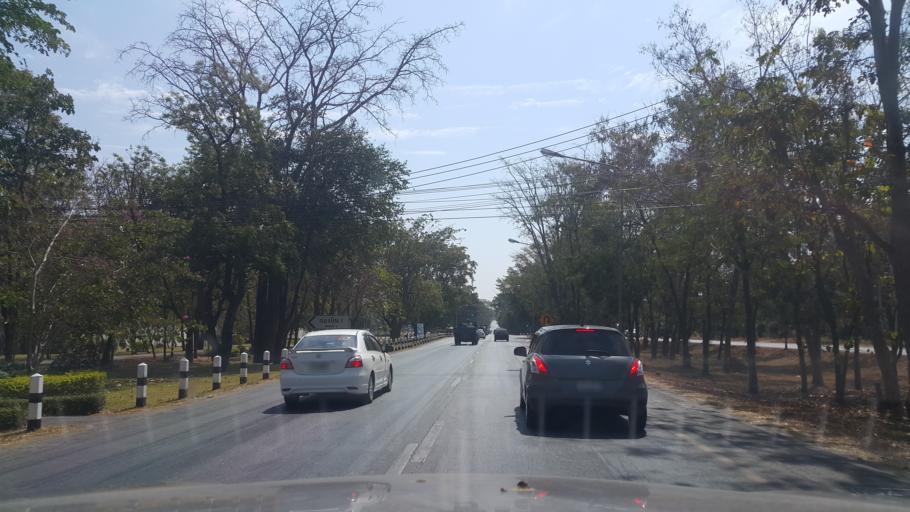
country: TH
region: Nakhon Ratchasima
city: Nakhon Ratchasima
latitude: 14.9236
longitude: 102.0611
